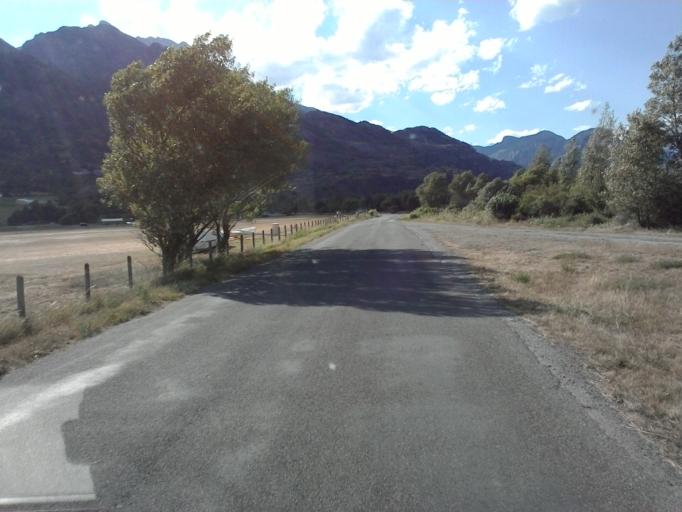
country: FR
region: Provence-Alpes-Cote d'Azur
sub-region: Departement des Hautes-Alpes
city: Guillestre
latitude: 44.7049
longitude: 6.5996
